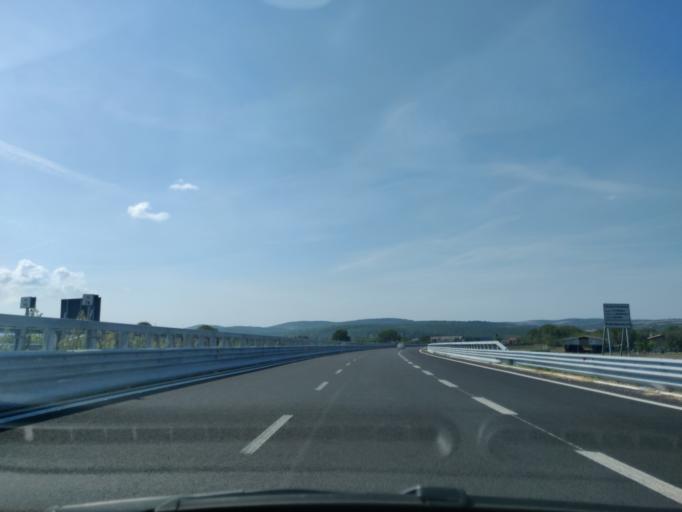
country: IT
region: Latium
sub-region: Provincia di Viterbo
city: Blera
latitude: 42.3049
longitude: 11.9875
